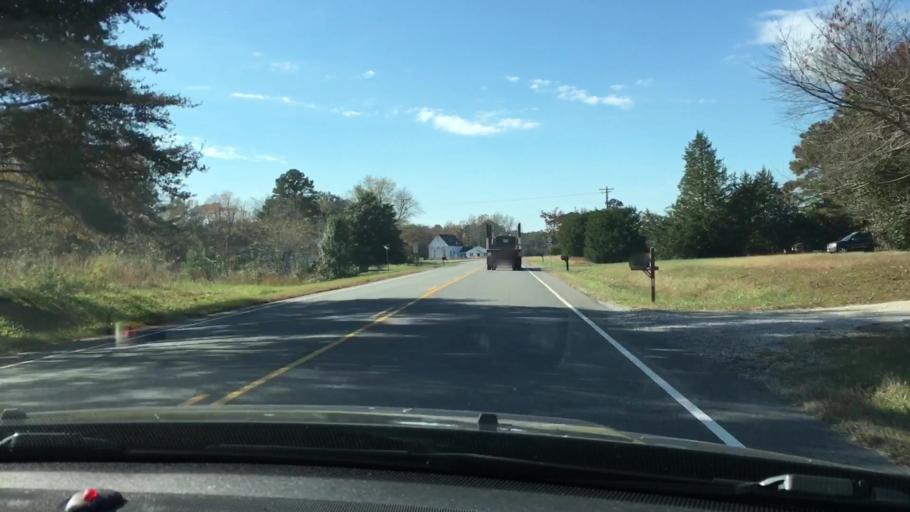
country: US
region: Virginia
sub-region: King William County
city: Central Garage
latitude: 37.7916
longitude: -77.2080
